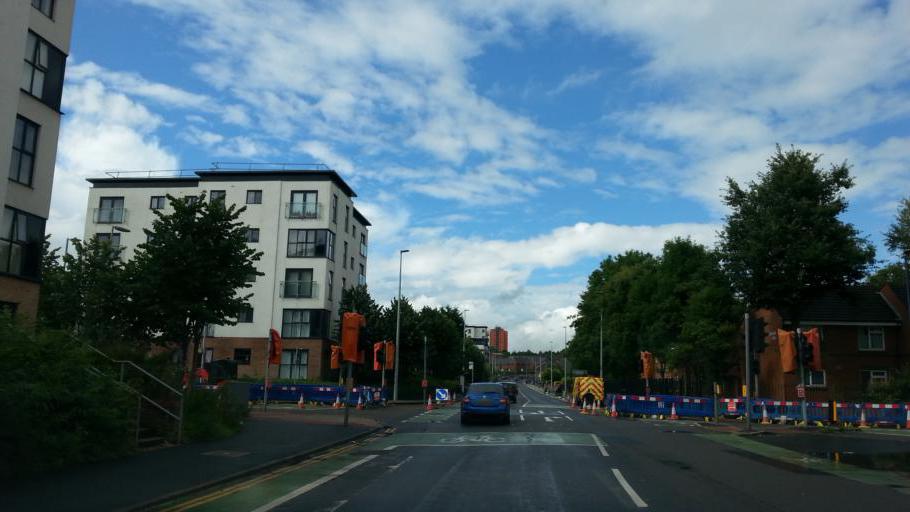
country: GB
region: England
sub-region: Manchester
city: Cheetham Hill
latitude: 53.4958
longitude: -2.2593
